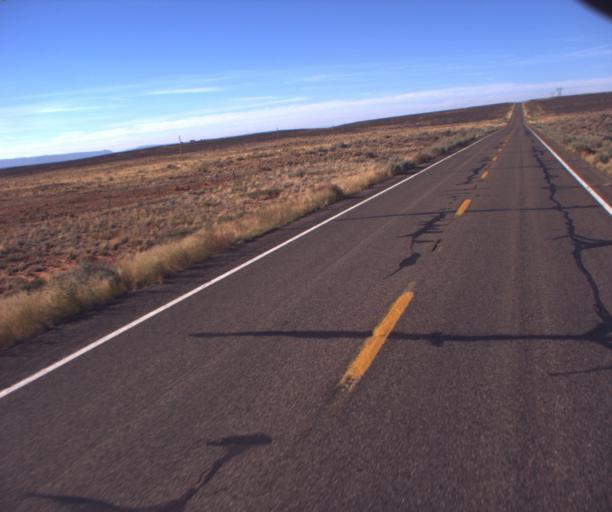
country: US
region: Arizona
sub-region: Coconino County
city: LeChee
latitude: 36.7850
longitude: -111.2927
